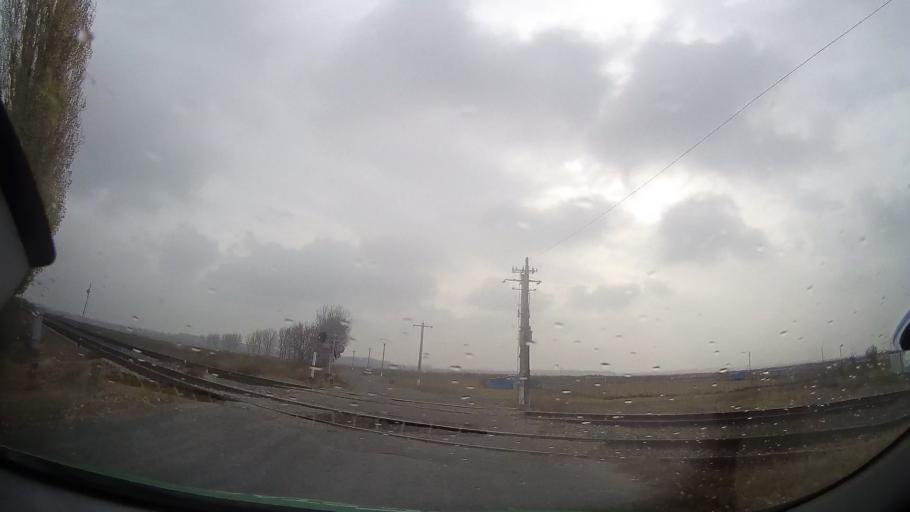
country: RO
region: Prahova
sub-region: Comuna Draganesti
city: Draganesti
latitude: 44.8369
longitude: 26.2695
